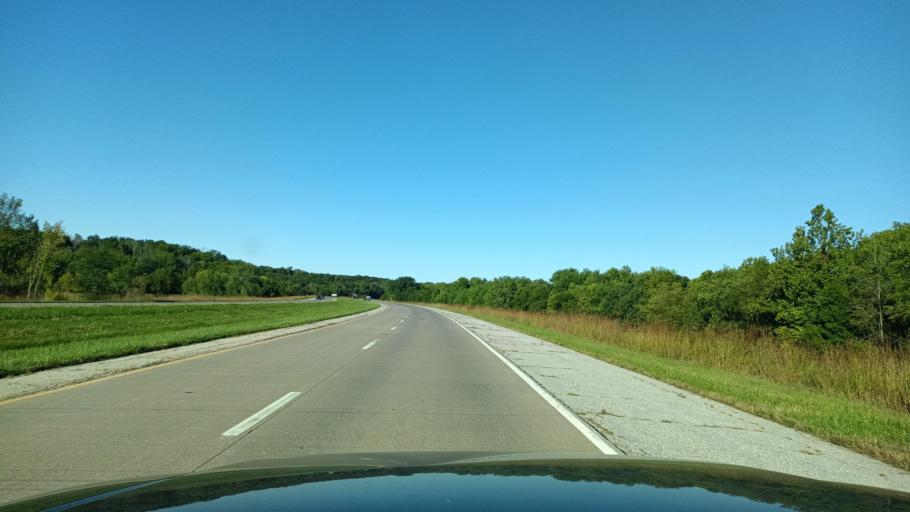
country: US
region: Illinois
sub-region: Warren County
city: Monmouth
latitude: 40.9224
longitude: -90.5348
